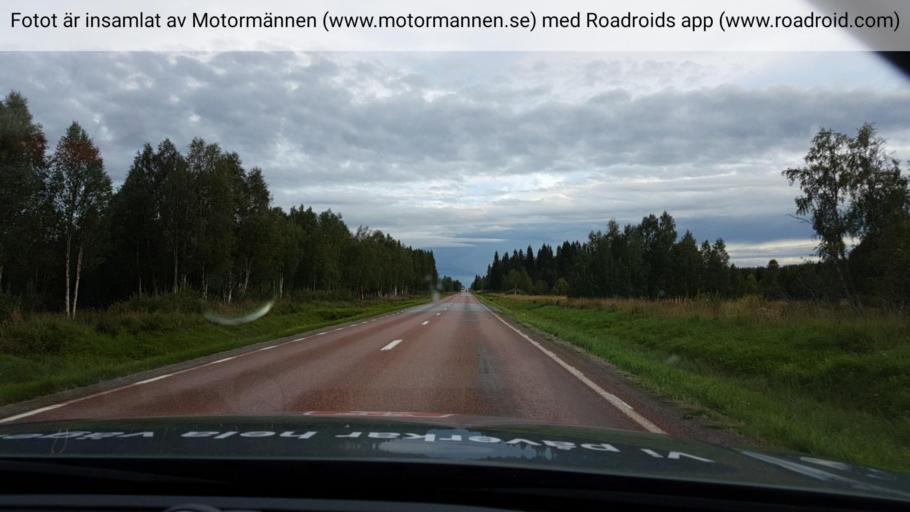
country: SE
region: Jaemtland
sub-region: Stroemsunds Kommun
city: Stroemsund
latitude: 63.7912
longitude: 15.5130
